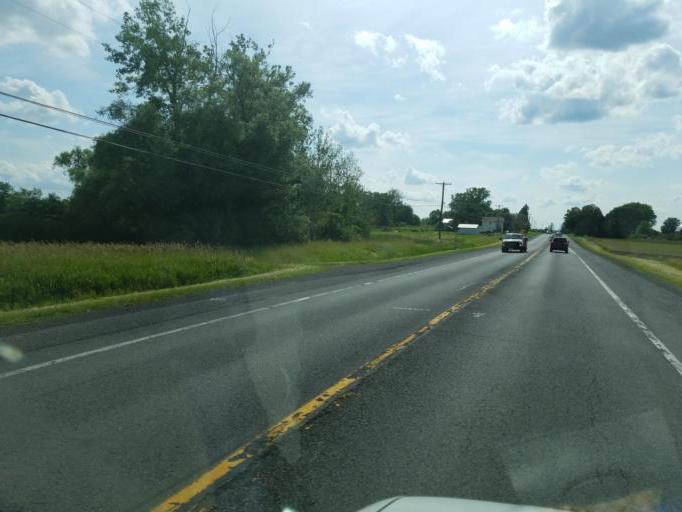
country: US
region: New York
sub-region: Ontario County
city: Clifton Springs
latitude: 42.8607
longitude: -77.1620
